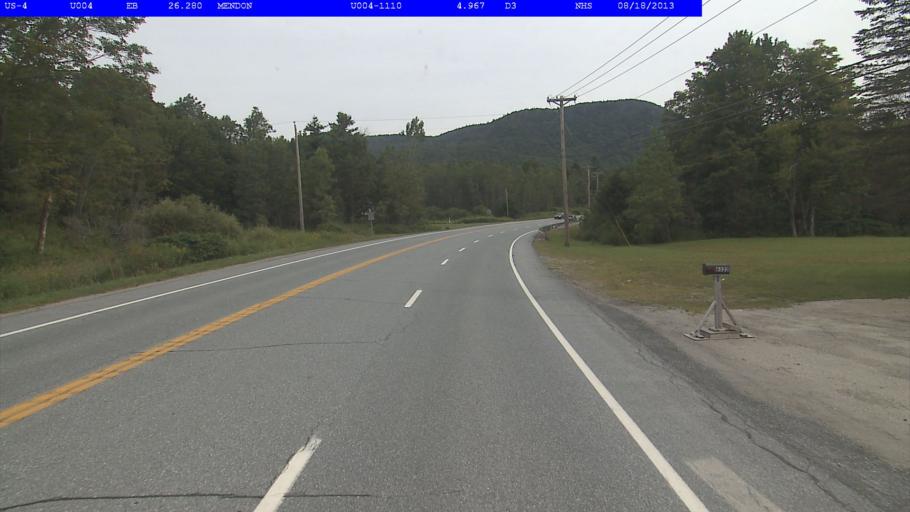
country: US
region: Vermont
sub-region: Rutland County
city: Rutland
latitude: 43.6647
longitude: -72.8636
